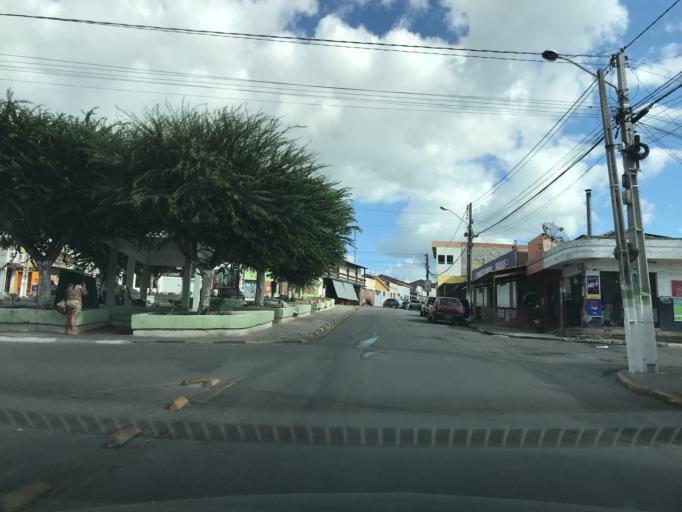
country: BR
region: Pernambuco
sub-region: Bezerros
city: Bezerros
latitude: -8.2376
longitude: -35.7531
